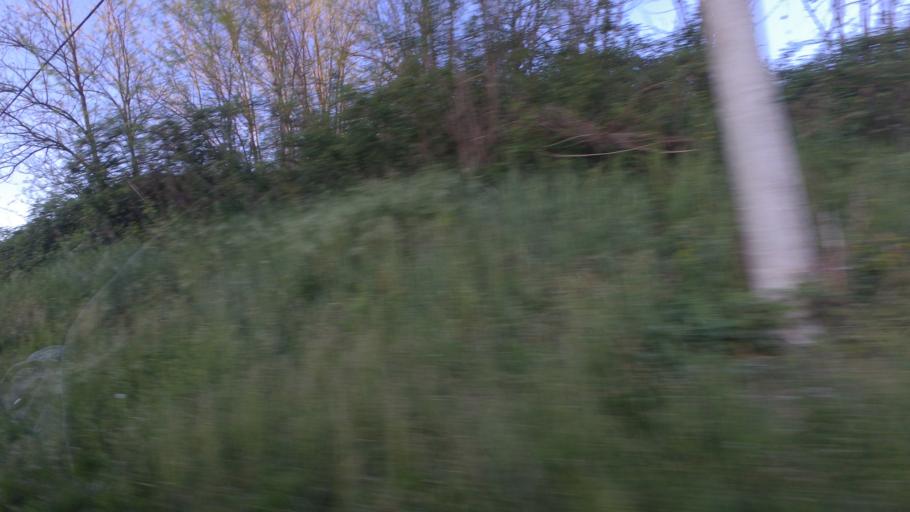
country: HR
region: Karlovacka
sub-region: Grad Karlovac
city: Karlovac
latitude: 45.4188
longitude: 15.5511
